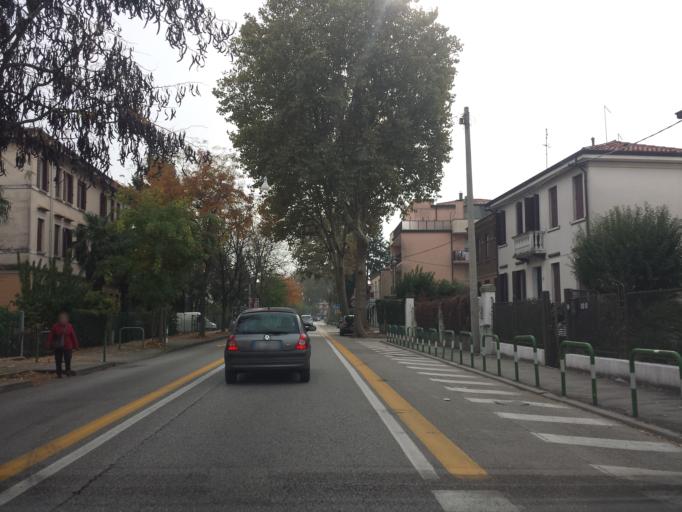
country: IT
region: Veneto
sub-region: Provincia di Padova
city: Padova
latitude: 45.4106
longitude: 11.8638
